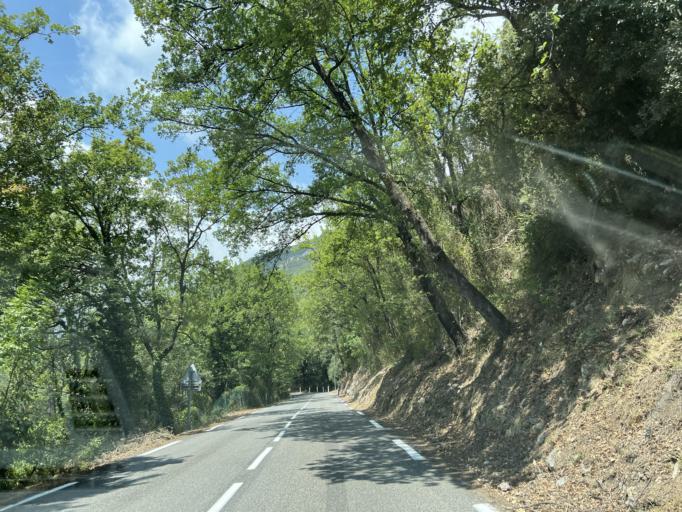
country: FR
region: Provence-Alpes-Cote d'Azur
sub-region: Departement des Alpes-Maritimes
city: Tourrettes-sur-Loup
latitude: 43.7063
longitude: 7.0315
